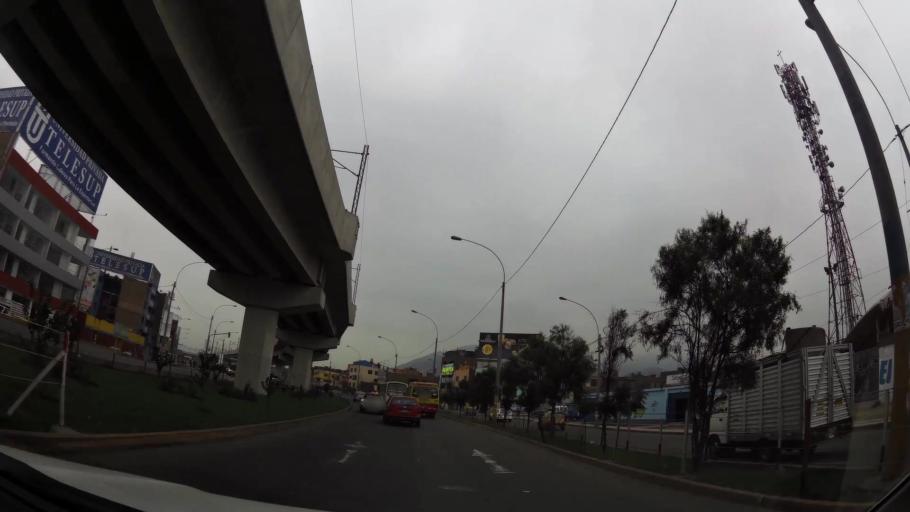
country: PE
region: Lima
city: Lima
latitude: -12.0168
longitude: -77.0018
